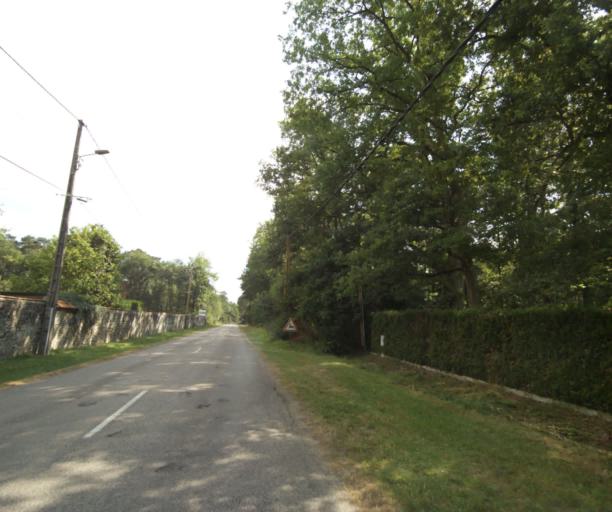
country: FR
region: Ile-de-France
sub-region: Departement de Seine-et-Marne
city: Arbonne-la-Foret
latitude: 48.4018
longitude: 2.5603
